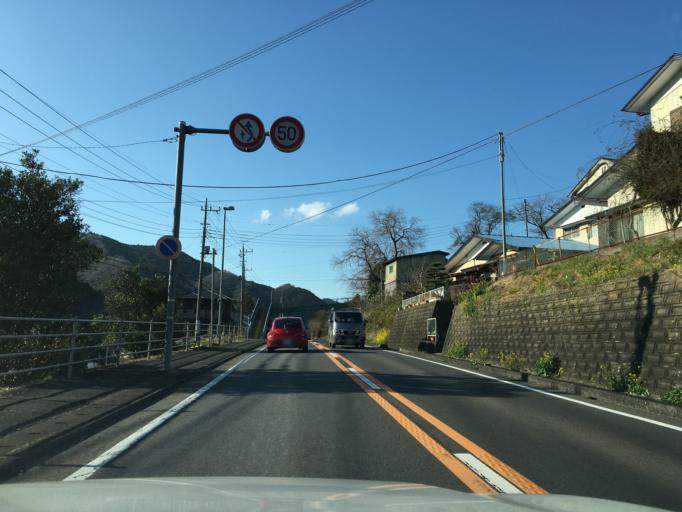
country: JP
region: Ibaraki
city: Daigo
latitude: 36.6962
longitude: 140.3868
